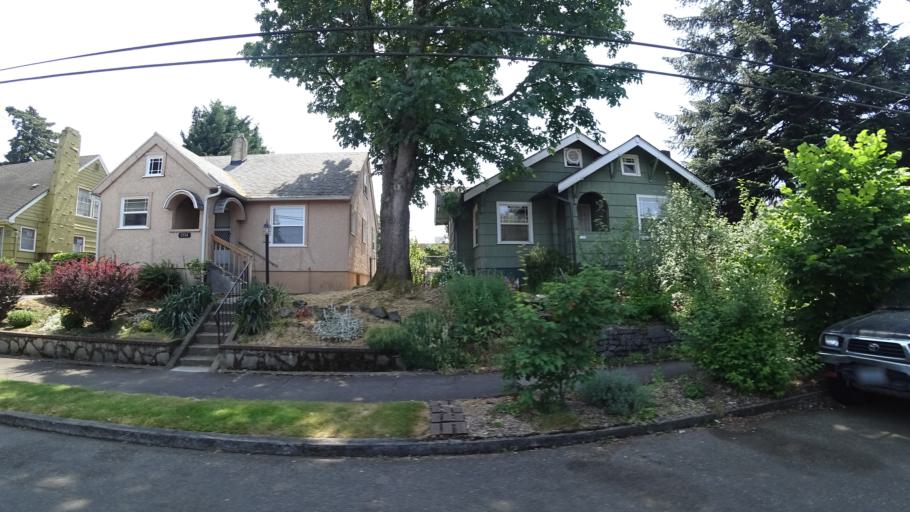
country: US
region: Oregon
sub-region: Multnomah County
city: Portland
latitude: 45.5780
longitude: -122.6812
